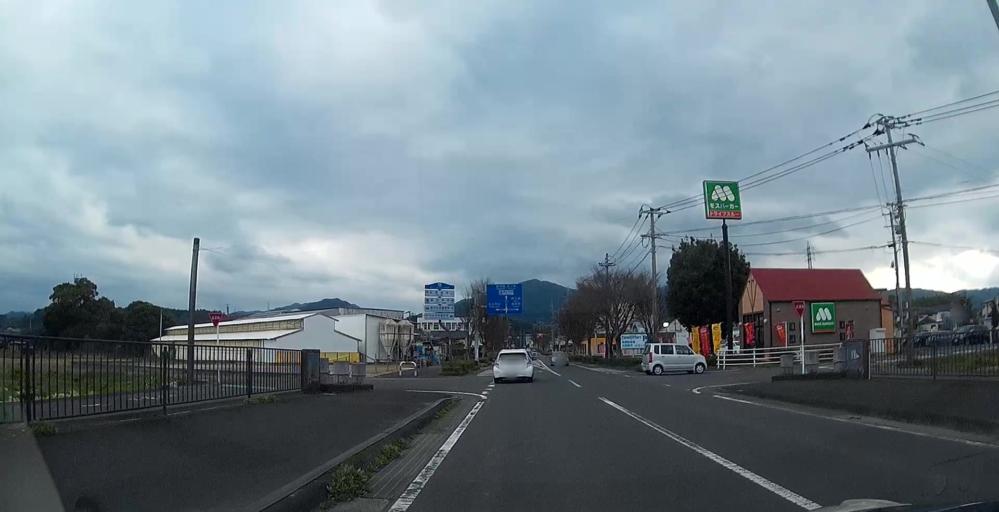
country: JP
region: Kagoshima
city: Izumi
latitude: 32.0758
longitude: 130.3472
